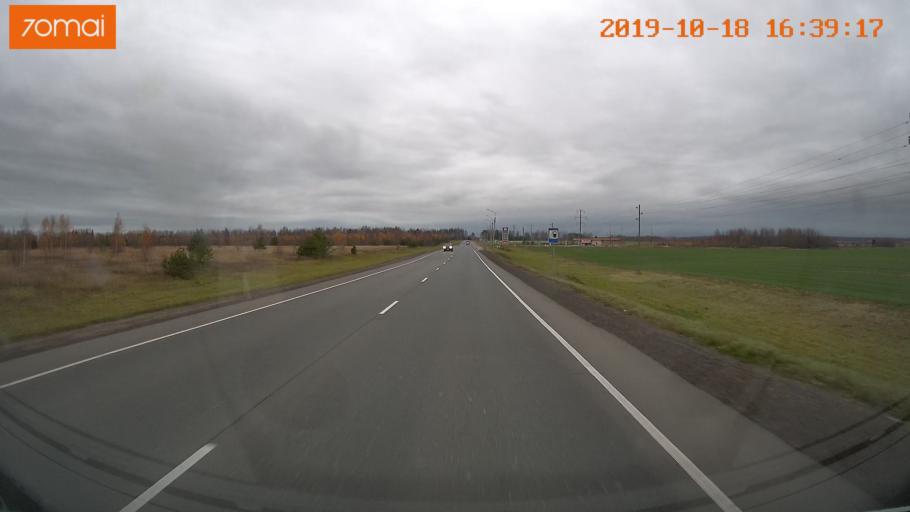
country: RU
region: Vladimir
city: Suzdal'
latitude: 56.4492
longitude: 40.4623
